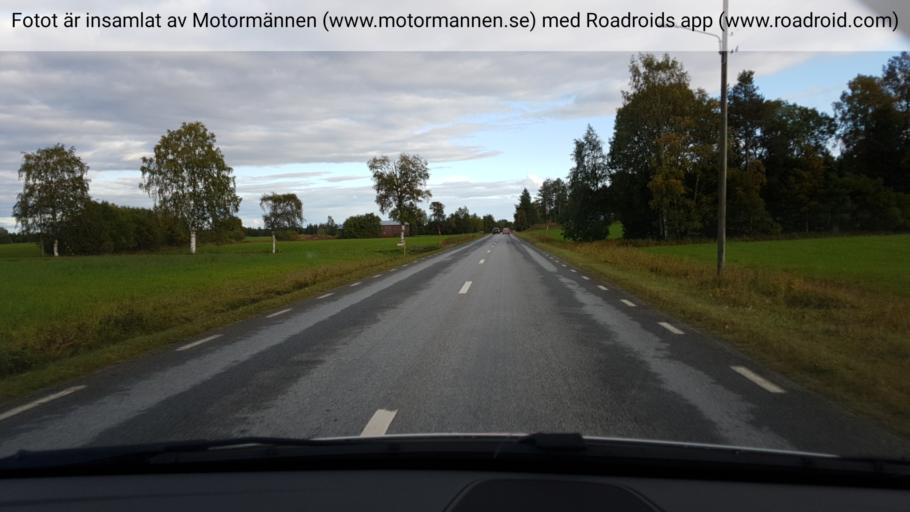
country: SE
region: Jaemtland
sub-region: Krokoms Kommun
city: Krokom
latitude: 63.1453
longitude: 14.1755
